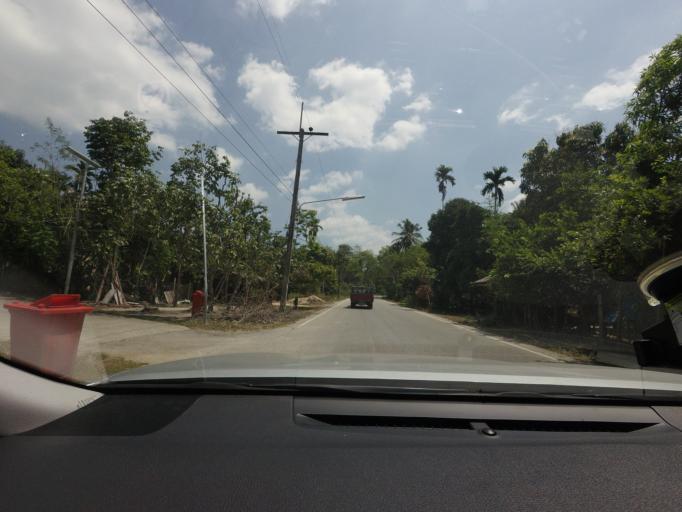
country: TH
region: Narathiwat
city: Rueso
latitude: 6.3889
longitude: 101.5062
